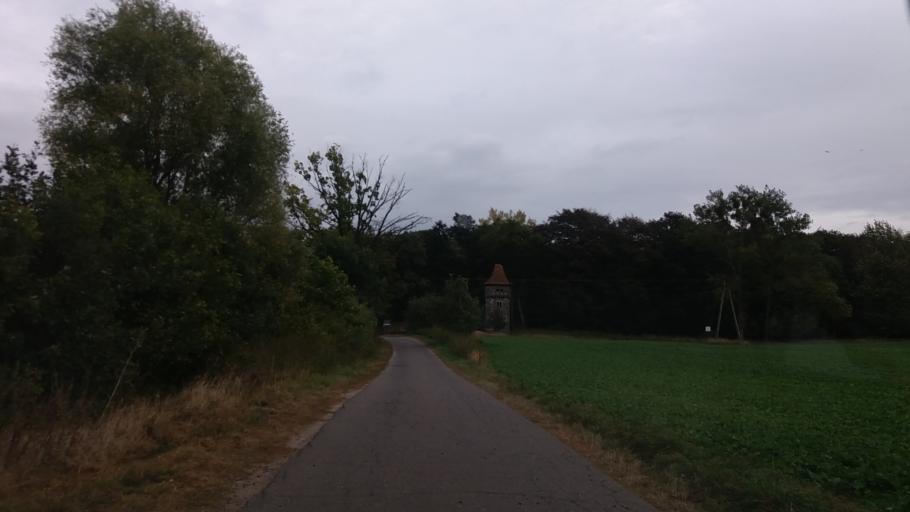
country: PL
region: West Pomeranian Voivodeship
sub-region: Powiat choszczenski
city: Krzecin
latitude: 52.9951
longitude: 15.5430
